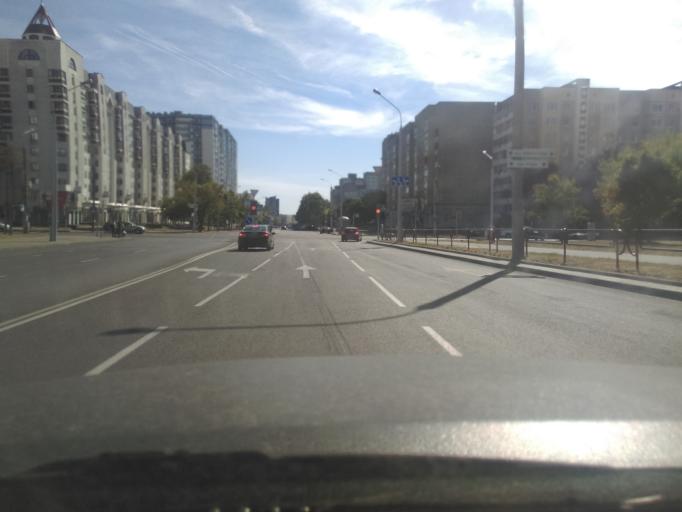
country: BY
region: Minsk
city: Minsk
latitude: 53.9333
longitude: 27.5904
